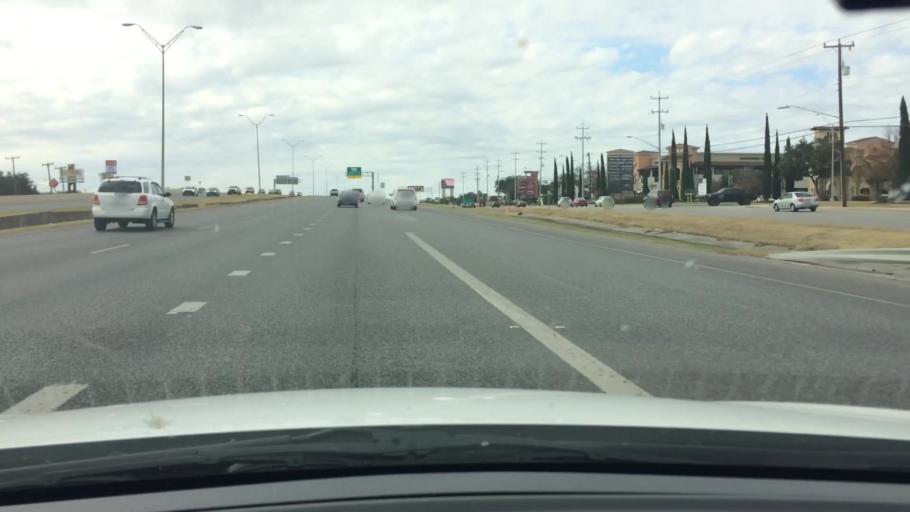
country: US
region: Texas
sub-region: Bexar County
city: Hollywood Park
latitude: 29.6103
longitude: -98.4882
